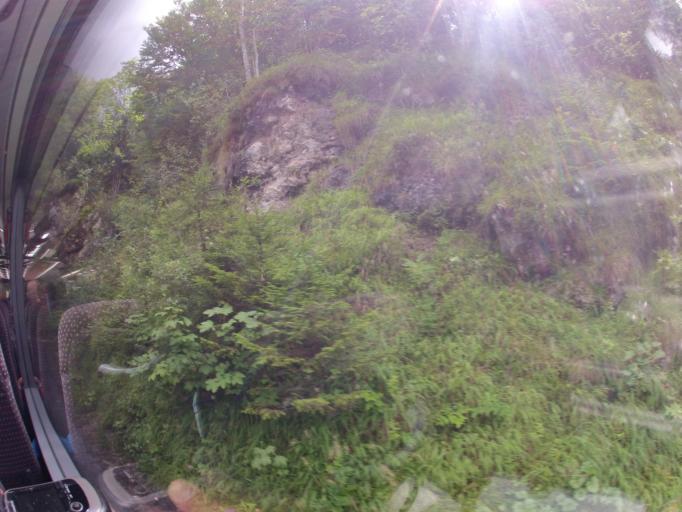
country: AT
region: Salzburg
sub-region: Politischer Bezirk Sankt Johann im Pongau
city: Werfen
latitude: 47.4929
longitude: 13.2000
